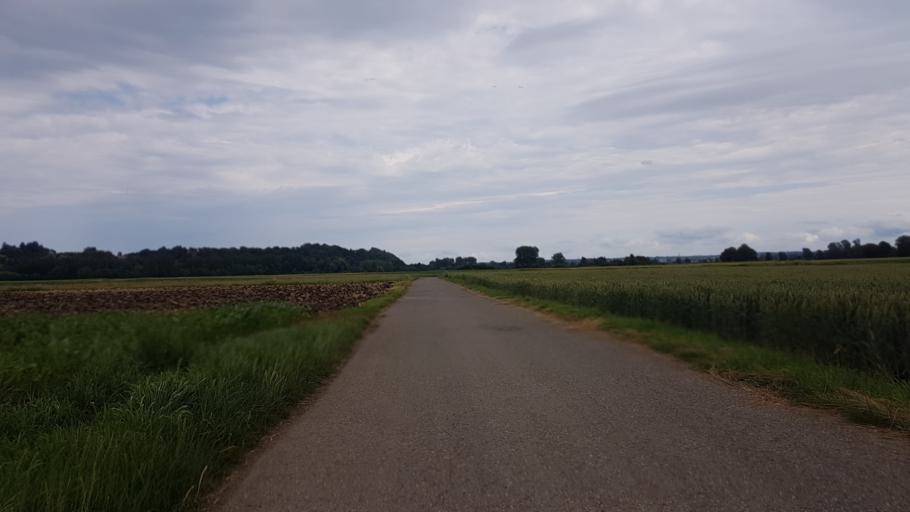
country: DE
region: Baden-Wuerttemberg
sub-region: Tuebingen Region
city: Mengen
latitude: 48.0635
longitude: 9.3626
